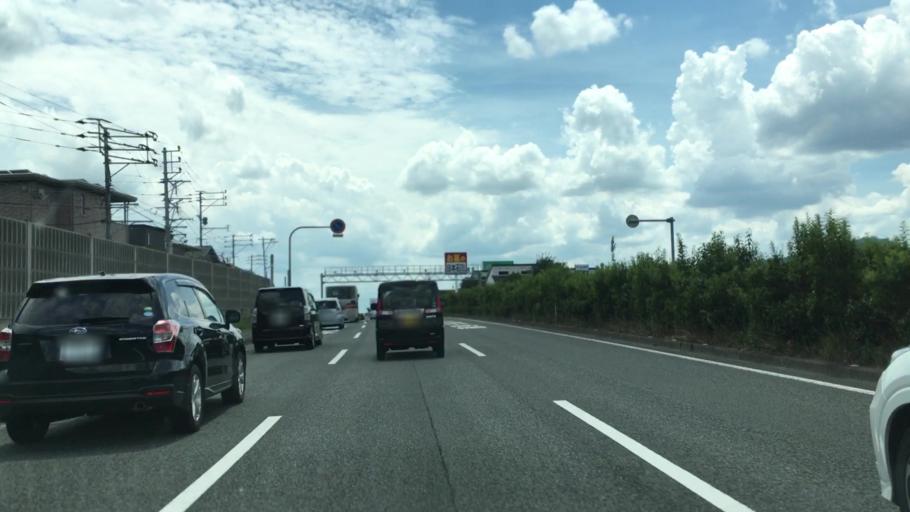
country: JP
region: Fukuoka
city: Chikushino-shi
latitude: 33.4907
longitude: 130.5354
